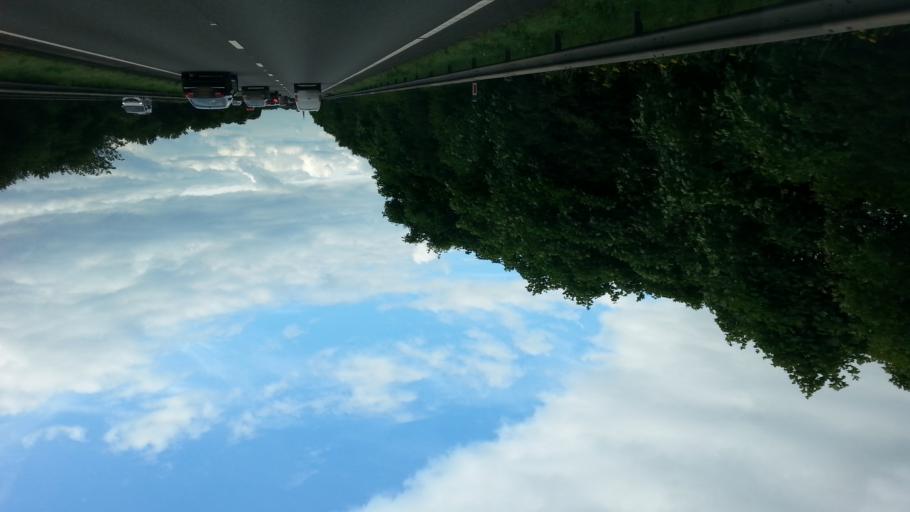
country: GB
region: England
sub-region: Nottinghamshire
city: South Collingham
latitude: 53.1791
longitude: -0.8186
